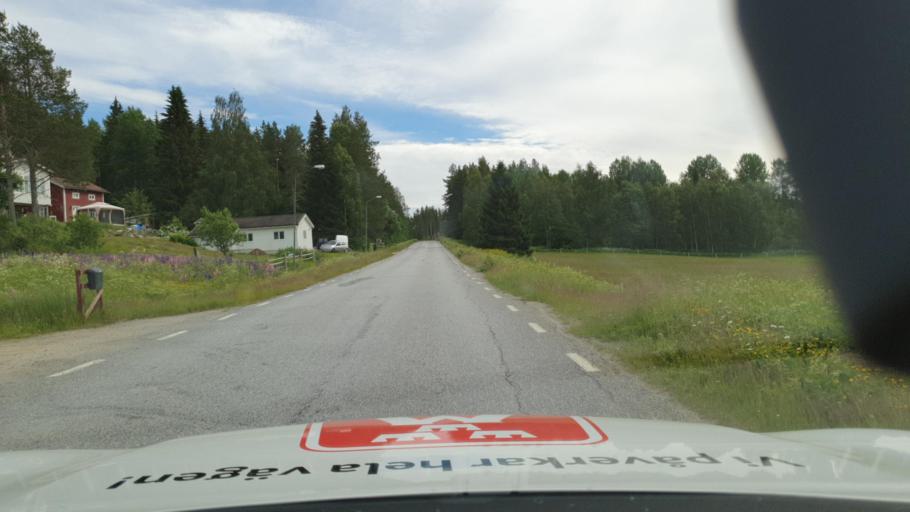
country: SE
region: Vaesterbotten
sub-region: Skelleftea Kommun
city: Burea
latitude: 64.4896
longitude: 21.0332
